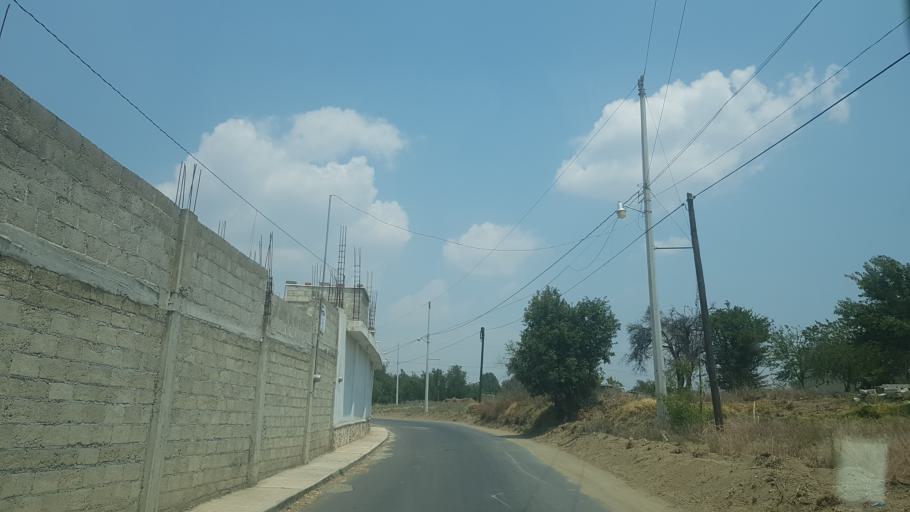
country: MX
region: Puebla
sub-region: San Nicolas de los Ranchos
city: San Pedro Yancuitlalpan
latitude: 19.0828
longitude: -98.4802
